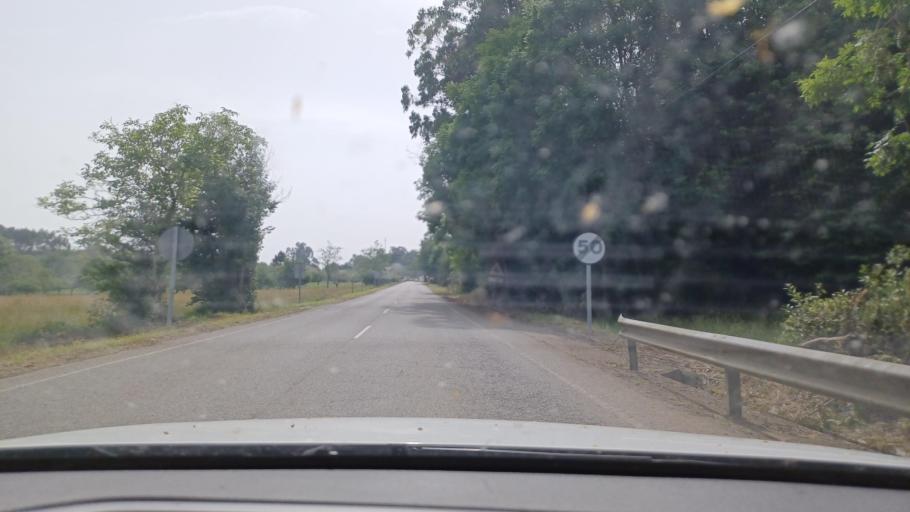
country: ES
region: Asturias
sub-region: Province of Asturias
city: Ribadesella
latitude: 43.4460
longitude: -5.0106
